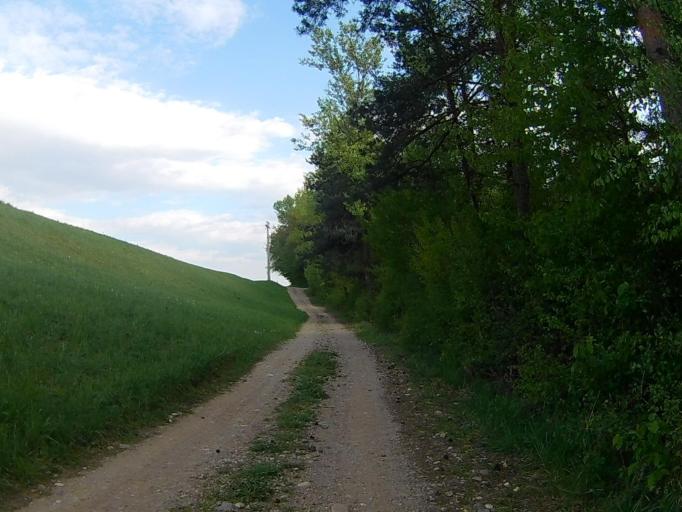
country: SI
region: Duplek
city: Spodnji Duplek
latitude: 46.4848
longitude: 15.7244
